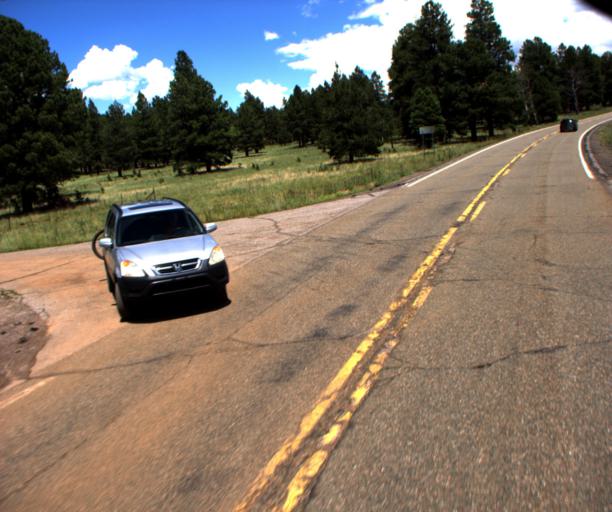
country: US
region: Arizona
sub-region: Coconino County
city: Parks
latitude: 35.3785
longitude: -111.7881
